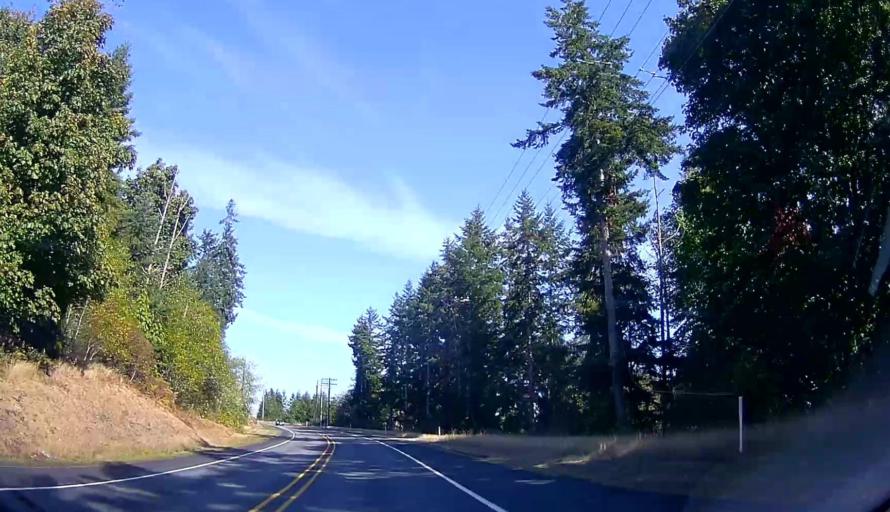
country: US
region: Washington
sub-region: Island County
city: Camano
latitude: 48.1909
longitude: -122.4931
